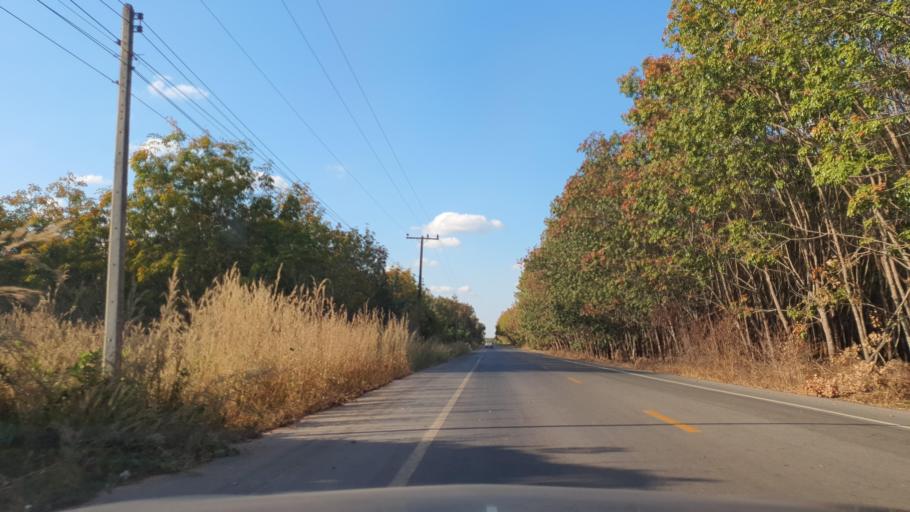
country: TH
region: Nong Khai
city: Bueng Khong Long
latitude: 18.0166
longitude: 104.0006
